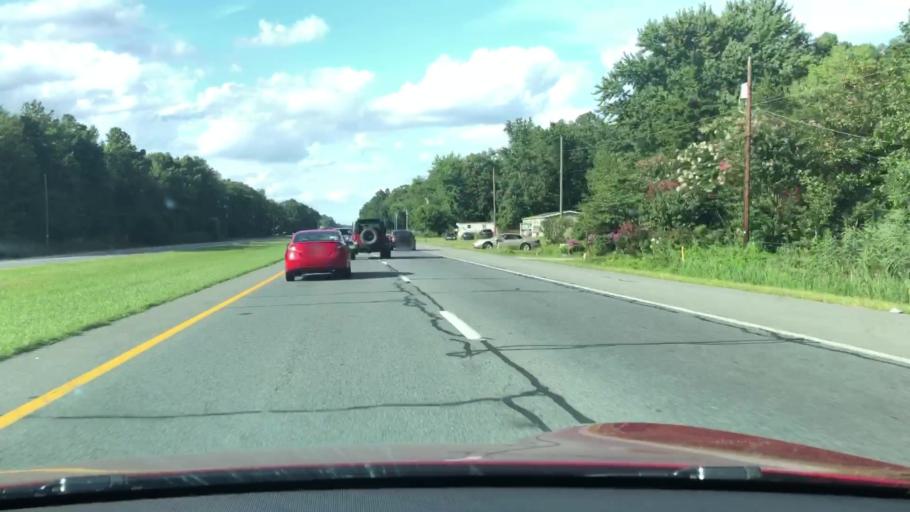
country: US
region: Delaware
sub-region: Kent County
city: Woodside East
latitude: 39.0610
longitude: -75.5548
